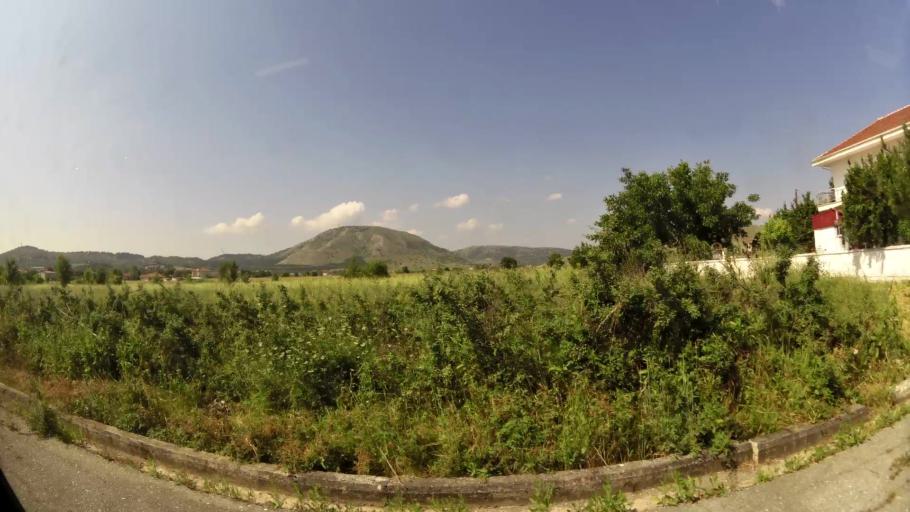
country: GR
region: West Macedonia
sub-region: Nomos Kozanis
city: Koila
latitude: 40.3362
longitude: 21.7871
